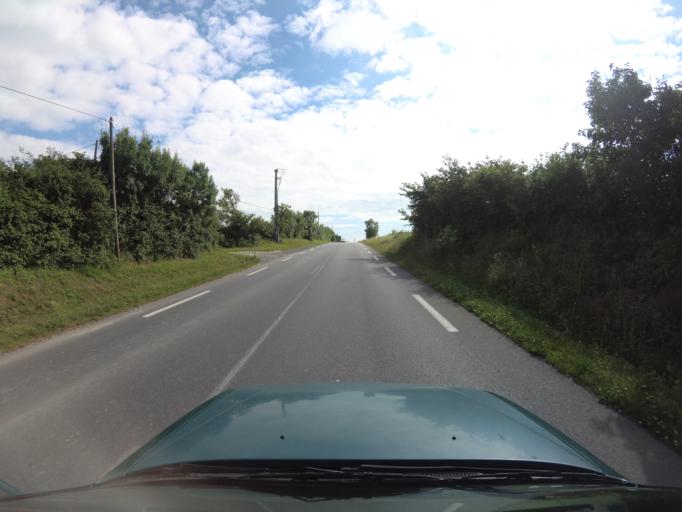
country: FR
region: Poitou-Charentes
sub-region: Departement de la Charente-Maritime
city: Saint-Xandre
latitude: 46.2276
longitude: -1.0809
